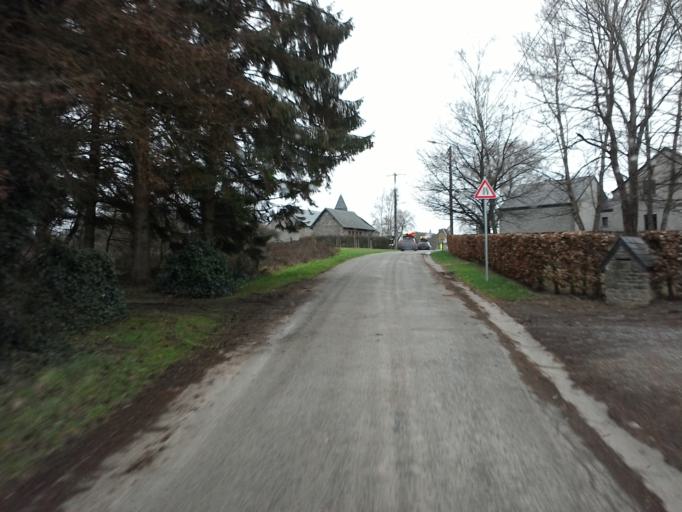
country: BE
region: Wallonia
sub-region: Province de Namur
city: Gedinne
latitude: 50.0237
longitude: 4.8605
